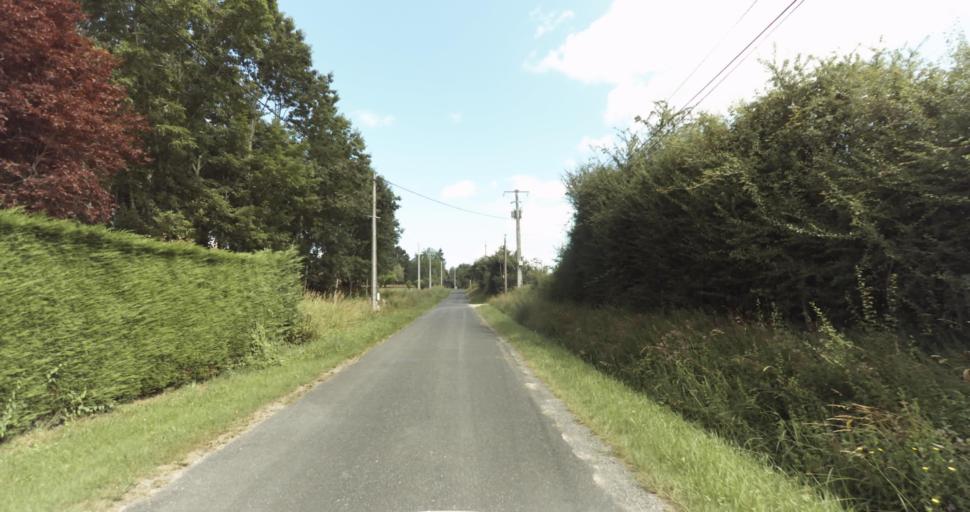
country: FR
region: Aquitaine
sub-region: Departement de la Gironde
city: Bazas
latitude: 44.4451
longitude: -0.2190
